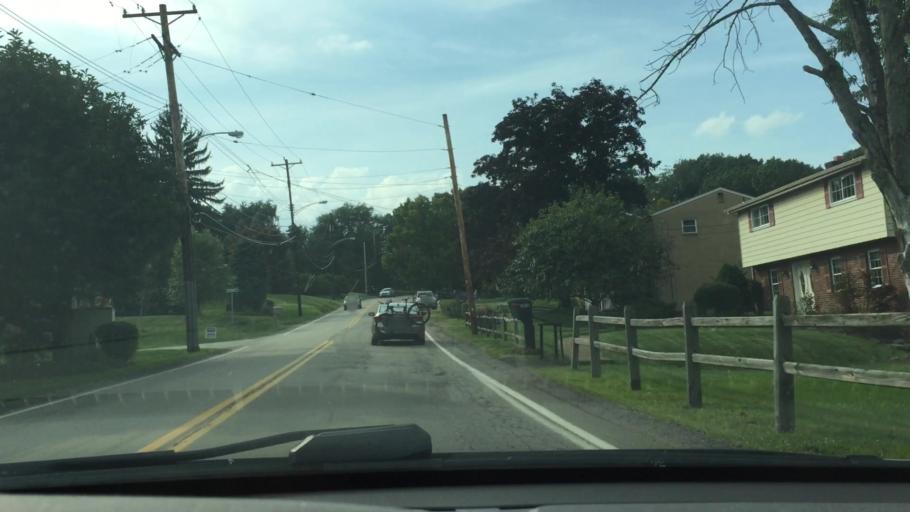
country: US
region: Pennsylvania
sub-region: Westmoreland County
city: Level Green
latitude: 40.4190
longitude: -79.7448
